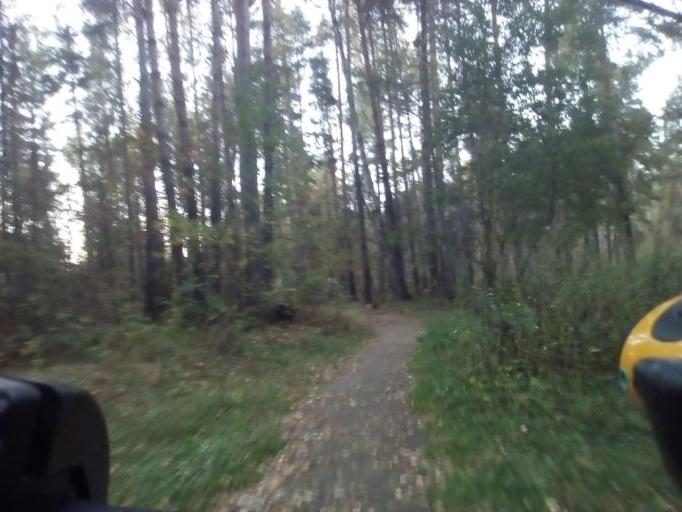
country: RU
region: Moskovskaya
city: Ramenskoye
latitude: 55.5930
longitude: 38.2154
